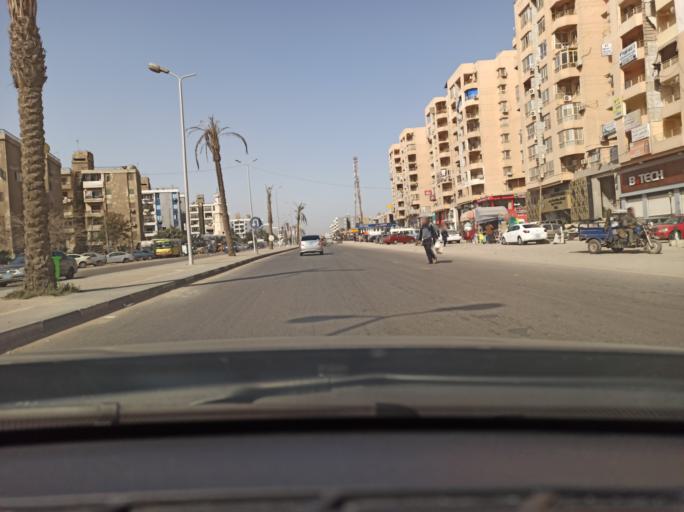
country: EG
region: Muhafazat al Qahirah
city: Cairo
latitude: 30.0510
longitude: 31.3968
